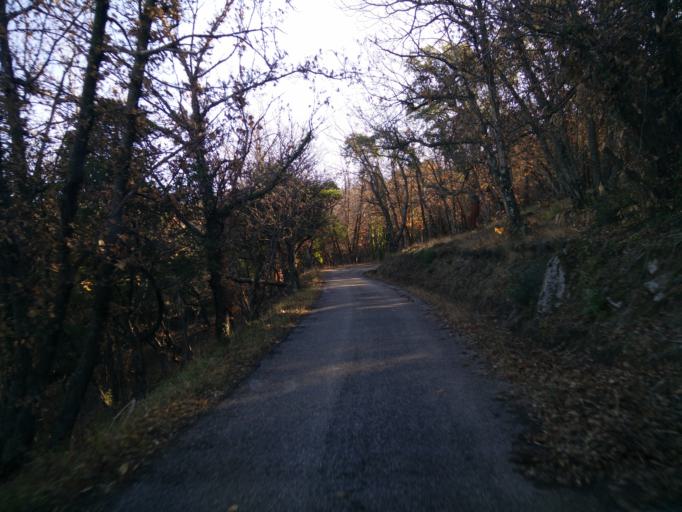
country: FR
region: Provence-Alpes-Cote d'Azur
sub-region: Departement du Var
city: Gonfaron
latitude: 43.2963
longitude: 6.2868
